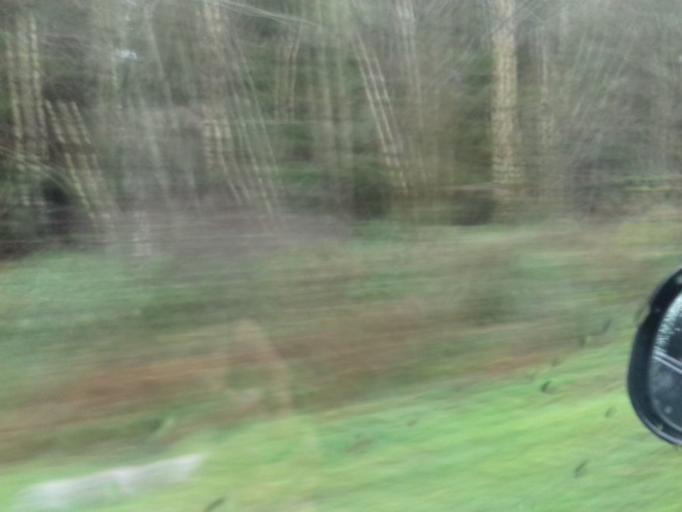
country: IE
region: Leinster
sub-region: Kilkenny
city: Graiguenamanagh
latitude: 52.5771
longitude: -6.9523
